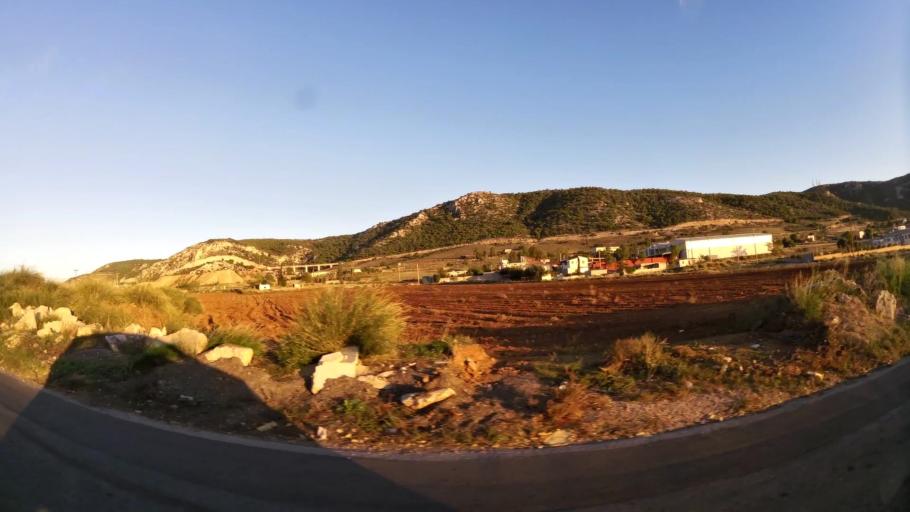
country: GR
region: Attica
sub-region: Nomarchia Athinas
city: Chaidari
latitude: 38.0468
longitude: 23.6377
